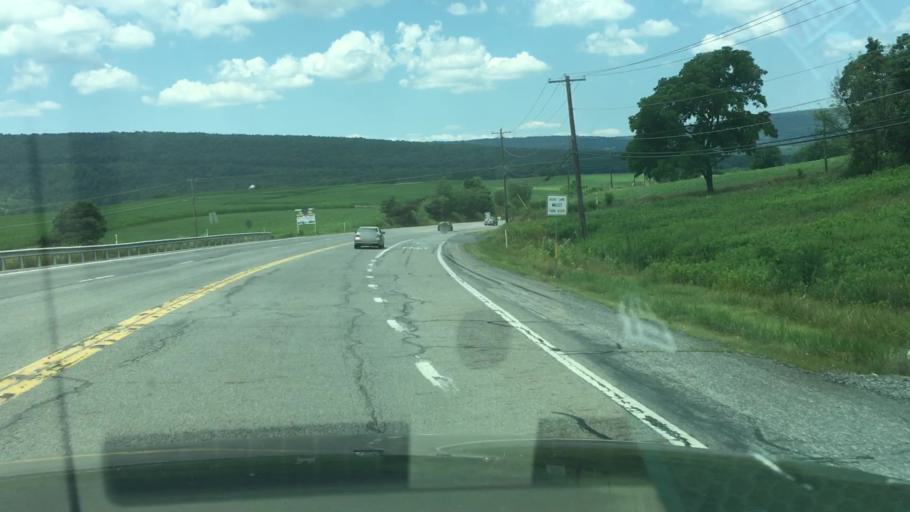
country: US
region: Pennsylvania
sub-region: Schuylkill County
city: Ashland
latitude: 40.7267
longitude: -76.3913
